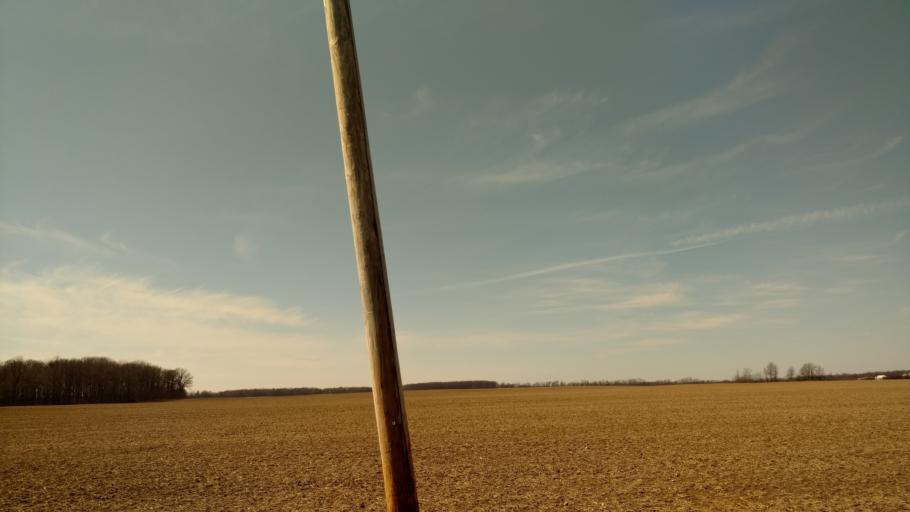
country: US
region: Ohio
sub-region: Union County
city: Richwood
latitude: 40.5191
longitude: -83.4532
